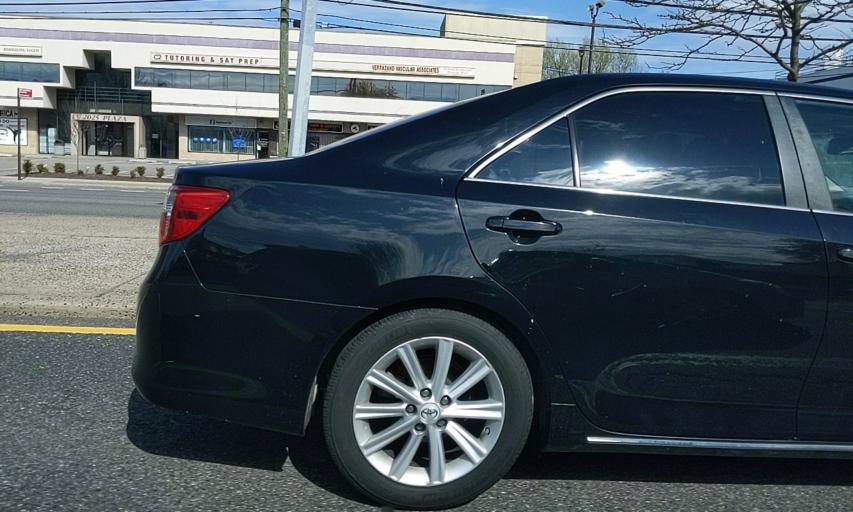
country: US
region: New York
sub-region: Richmond County
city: Bloomfield
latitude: 40.5979
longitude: -74.1625
